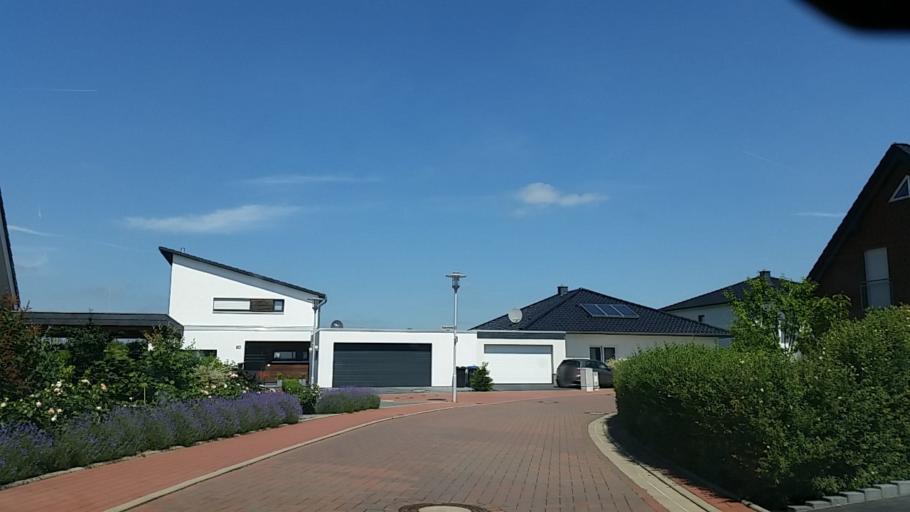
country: DE
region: Lower Saxony
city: Weyhausen
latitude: 52.4020
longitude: 10.7184
